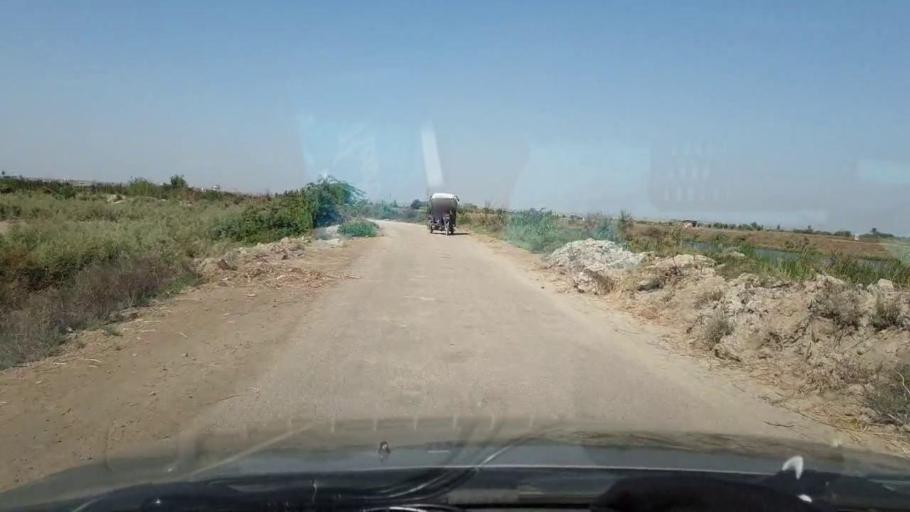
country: PK
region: Sindh
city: Thatta
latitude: 24.6362
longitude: 67.9024
